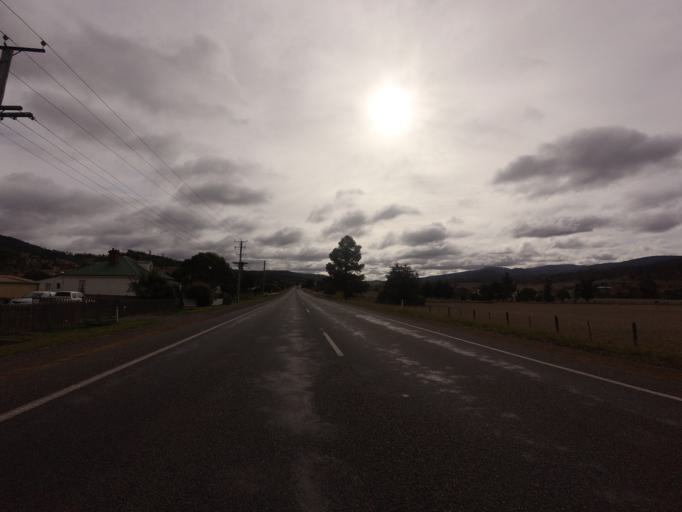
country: AU
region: Tasmania
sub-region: Brighton
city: Bridgewater
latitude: -42.6415
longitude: 147.2297
